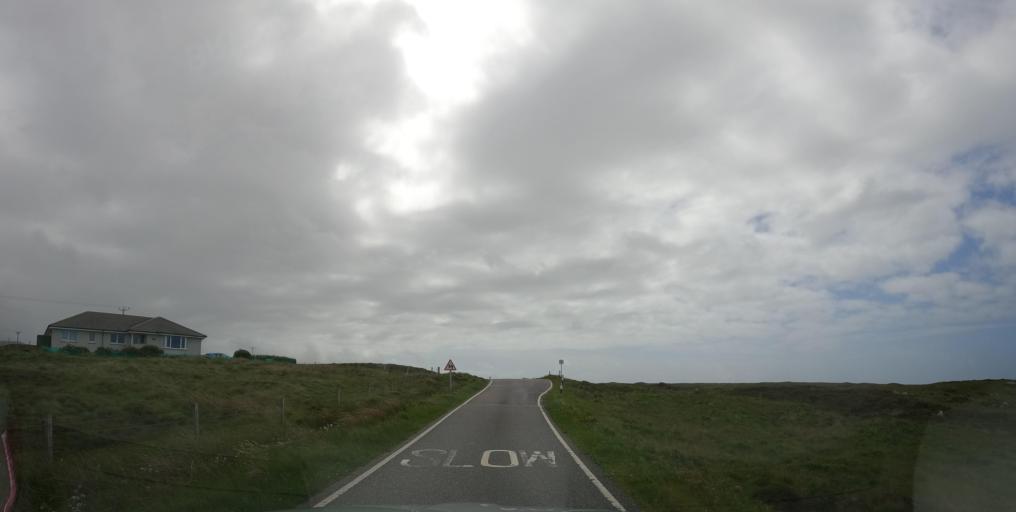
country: GB
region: Scotland
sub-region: Eilean Siar
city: Isle of South Uist
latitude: 57.2833
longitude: -7.3663
